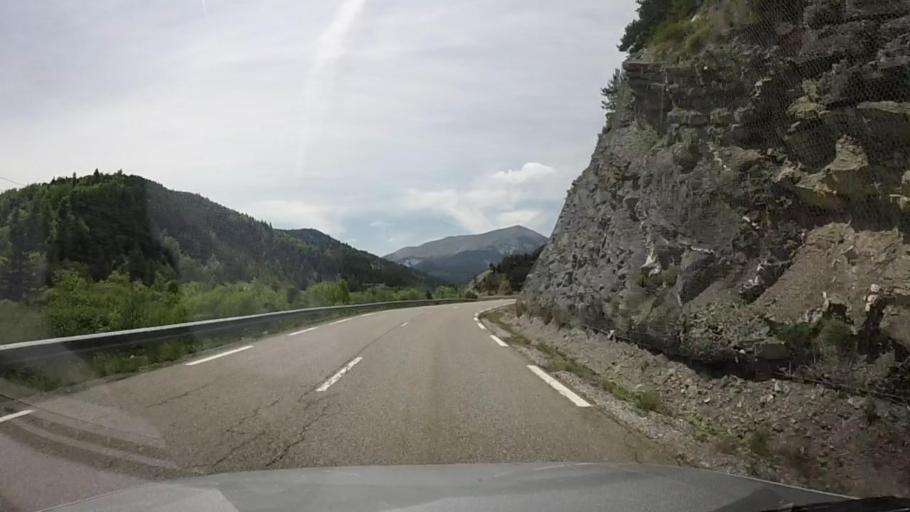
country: FR
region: Provence-Alpes-Cote d'Azur
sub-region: Departement des Alpes-de-Haute-Provence
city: Seyne-les-Alpes
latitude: 44.2733
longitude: 6.3847
